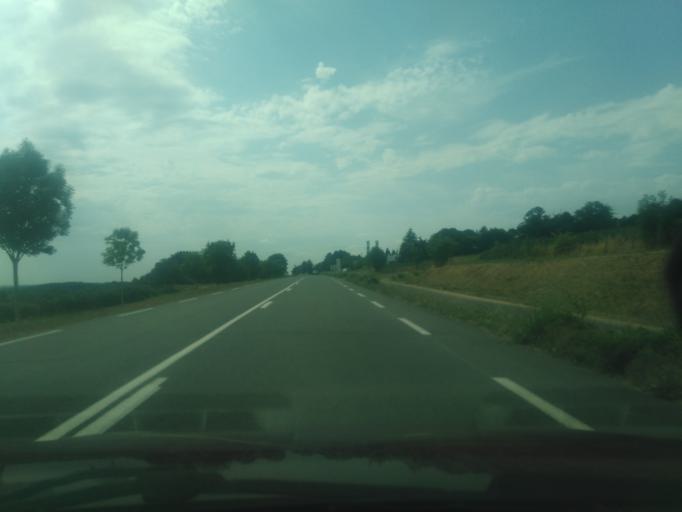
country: FR
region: Pays de la Loire
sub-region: Departement de la Vendee
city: Antigny
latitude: 46.6582
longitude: -0.7770
